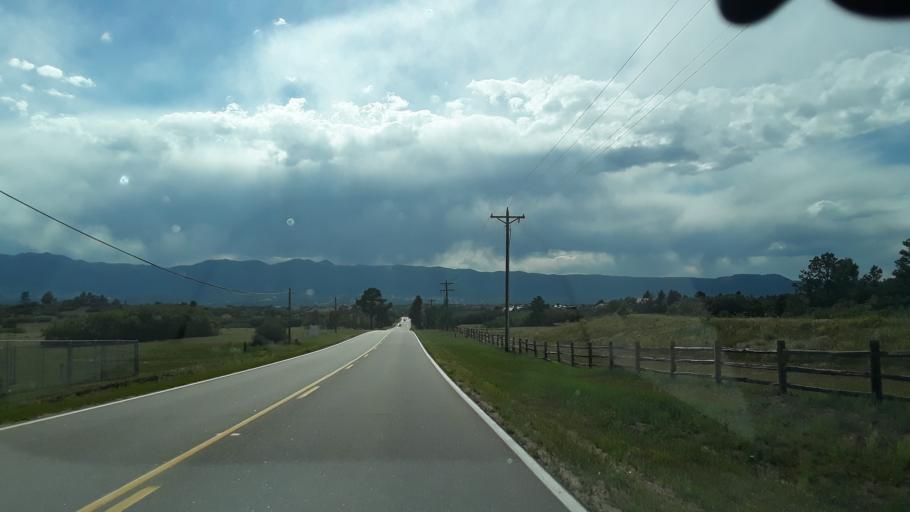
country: US
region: Colorado
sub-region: El Paso County
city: Black Forest
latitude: 39.0128
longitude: -104.7545
